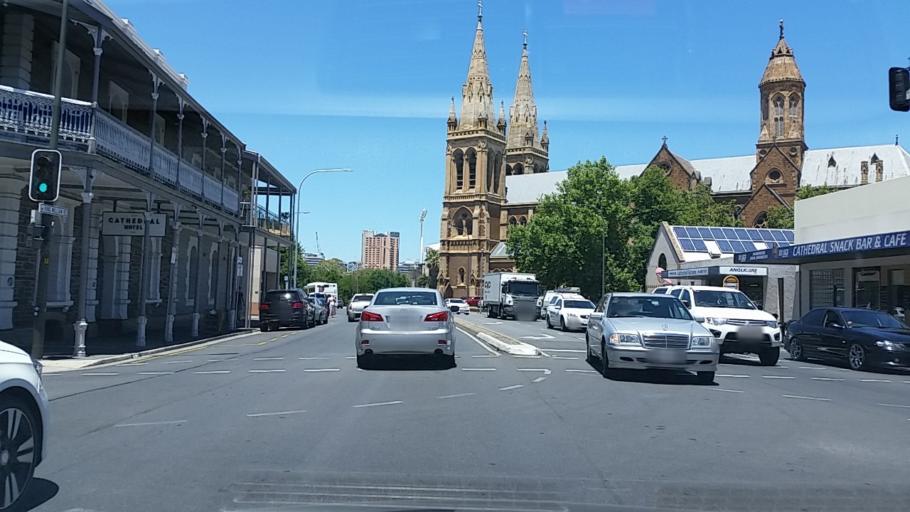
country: AU
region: South Australia
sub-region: Adelaide
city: North Adelaide
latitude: -34.9119
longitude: 138.5989
